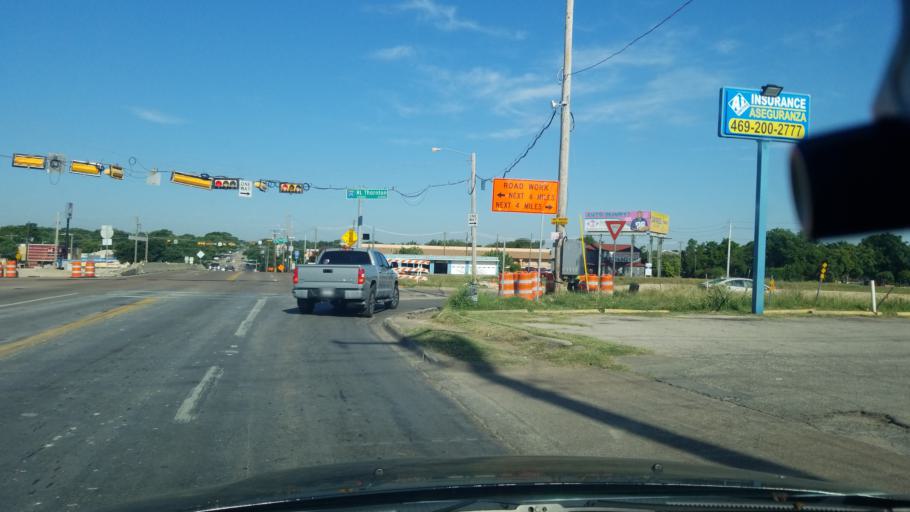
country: US
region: Texas
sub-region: Dallas County
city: Cockrell Hill
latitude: 32.7205
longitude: -96.8266
